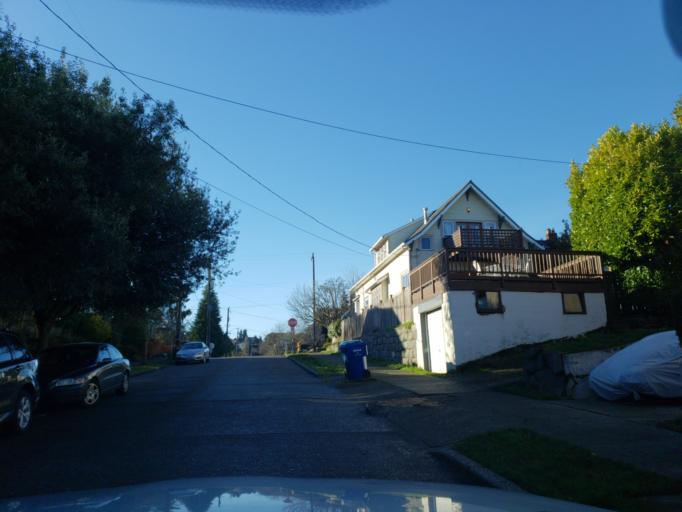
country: US
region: Washington
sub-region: King County
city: Seattle
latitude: 47.6796
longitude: -122.3465
